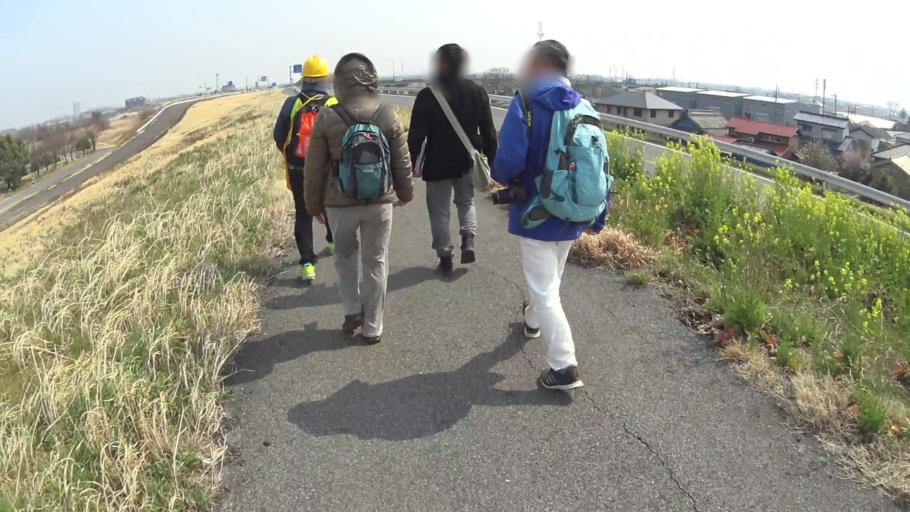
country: JP
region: Ibaraki
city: Koga
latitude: 36.2022
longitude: 139.6736
